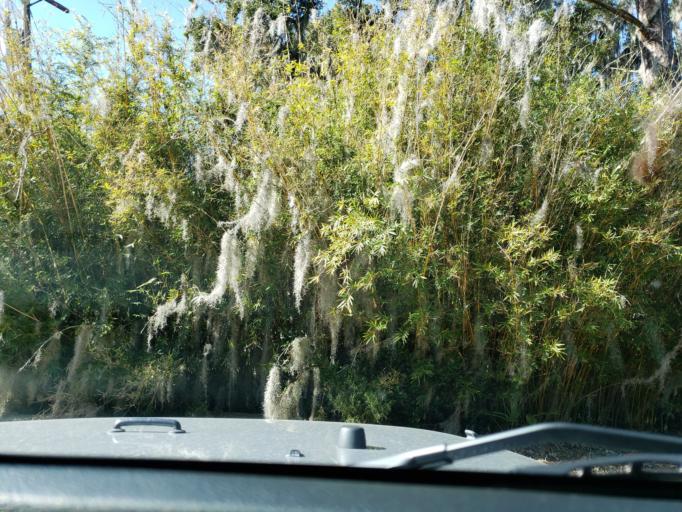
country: US
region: Georgia
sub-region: Chatham County
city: Whitemarsh Island
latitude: 32.0418
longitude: -80.9872
